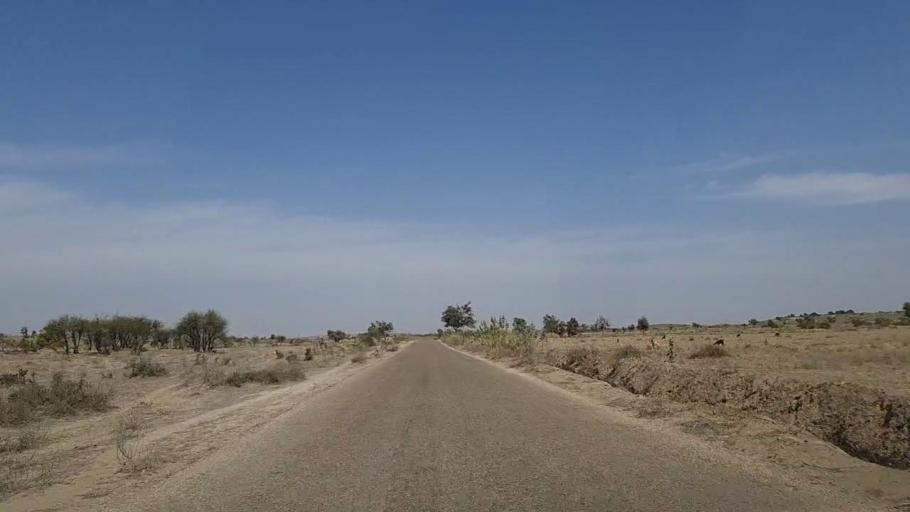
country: PK
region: Sindh
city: Nabisar
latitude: 25.0694
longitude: 69.9708
